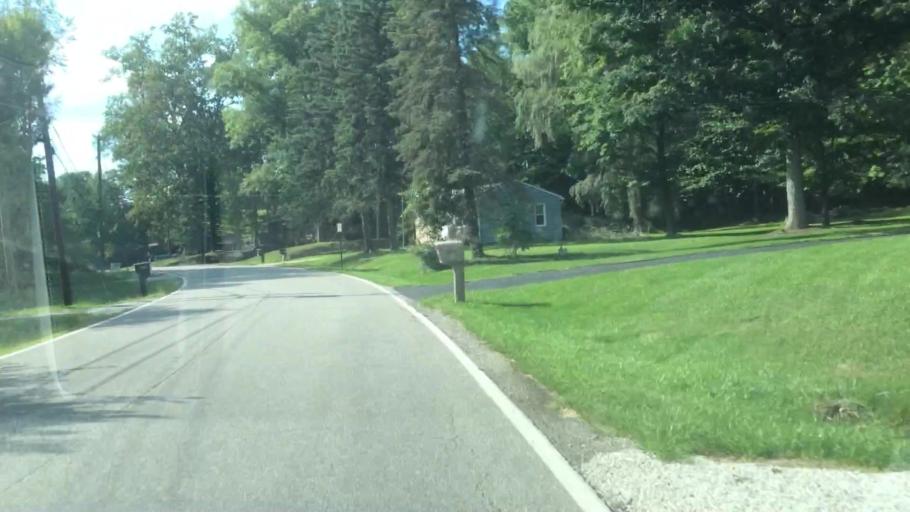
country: US
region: Ohio
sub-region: Summit County
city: Hudson
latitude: 41.2003
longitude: -81.4486
